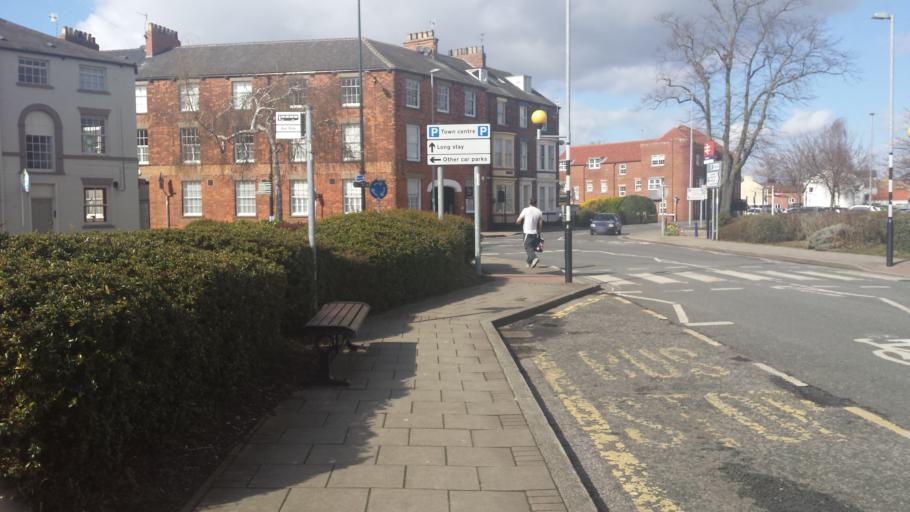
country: GB
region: England
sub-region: East Riding of Yorkshire
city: Beverley
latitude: 53.8418
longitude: -0.4238
